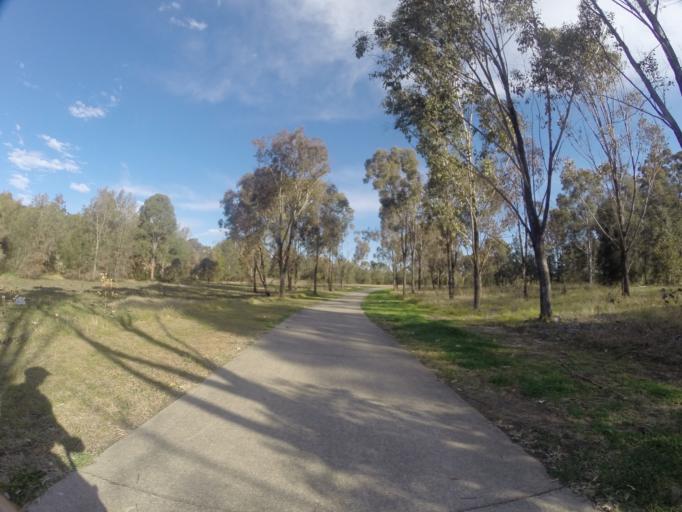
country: AU
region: New South Wales
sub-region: Fairfield
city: Horsley Park
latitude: -33.8530
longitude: 150.8743
